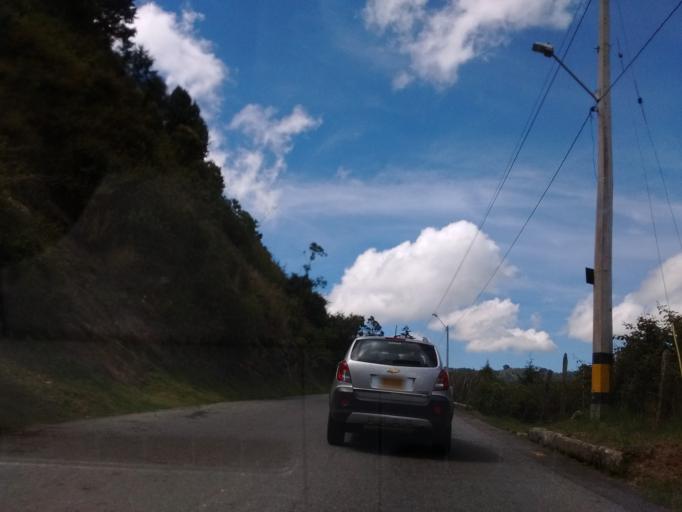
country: CO
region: Antioquia
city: Medellin
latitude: 6.2381
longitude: -75.5111
